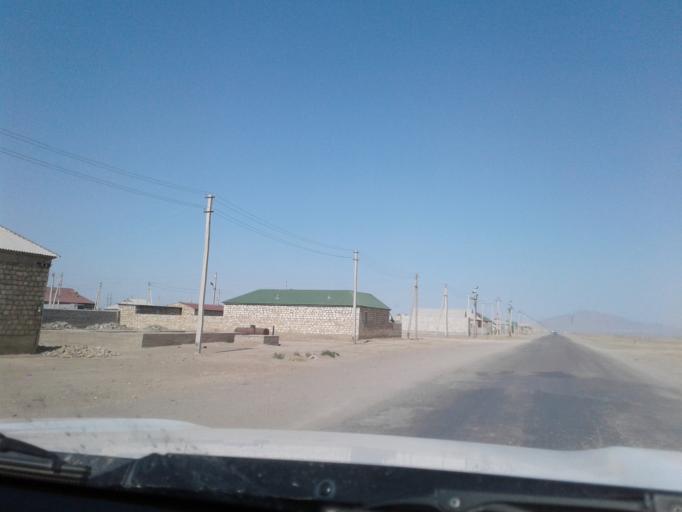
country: TM
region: Balkan
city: Gumdag
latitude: 39.1984
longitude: 54.6023
